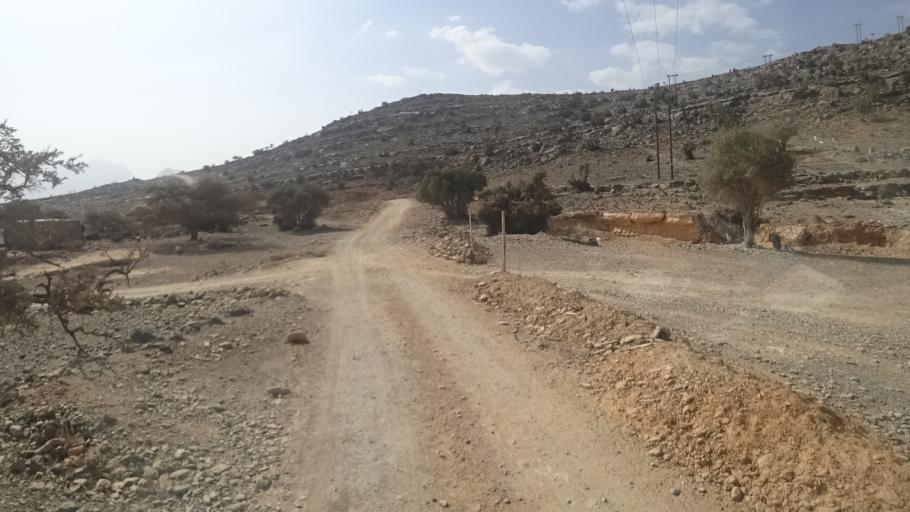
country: OM
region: Muhafazat ad Dakhiliyah
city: Bahla'
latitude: 23.1939
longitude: 57.2009
